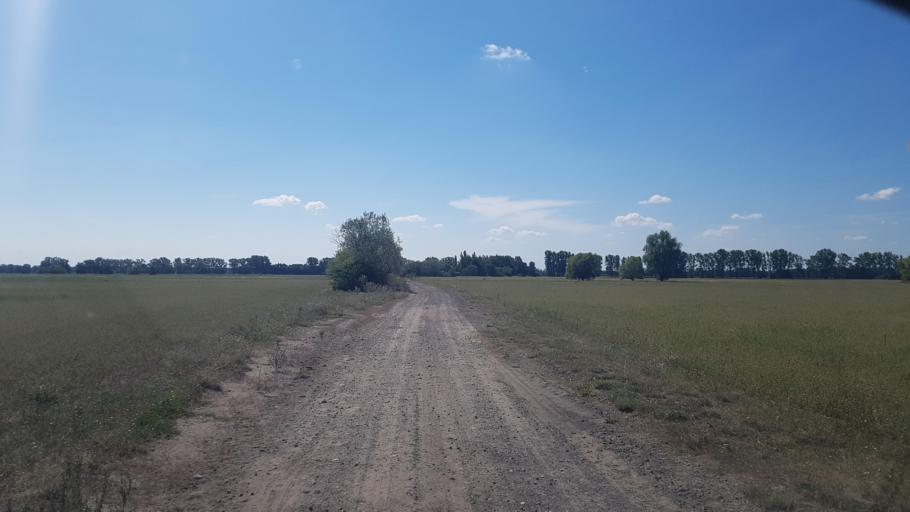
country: DE
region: Brandenburg
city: Golzow
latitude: 52.2540
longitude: 12.6626
